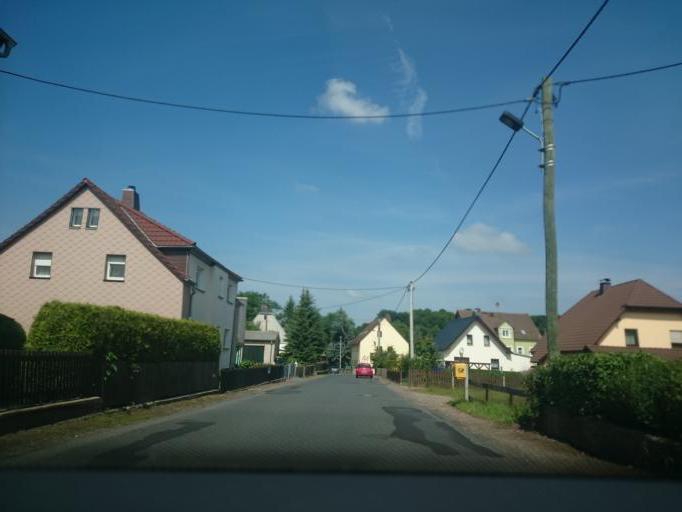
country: DE
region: Saxony
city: Brand-Erbisdorf
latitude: 50.8677
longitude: 13.3127
